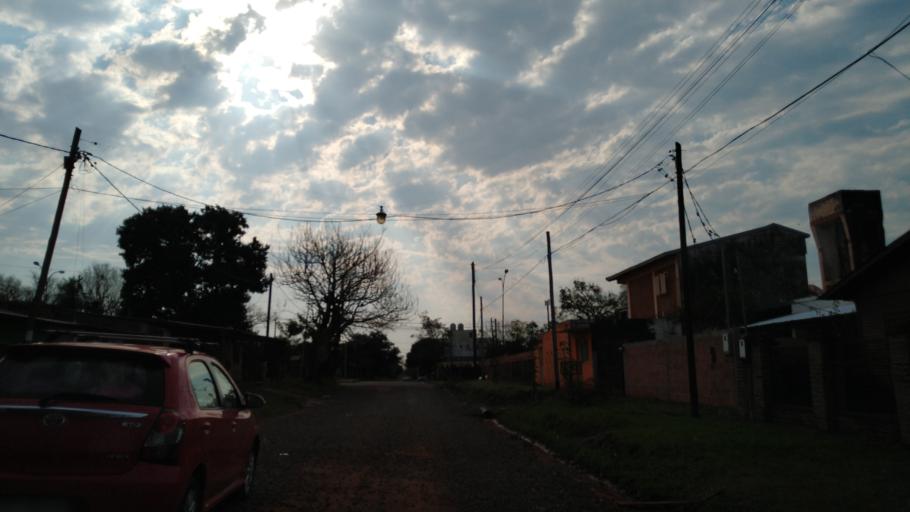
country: AR
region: Misiones
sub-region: Departamento de Capital
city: Posadas
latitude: -27.4293
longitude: -55.8797
